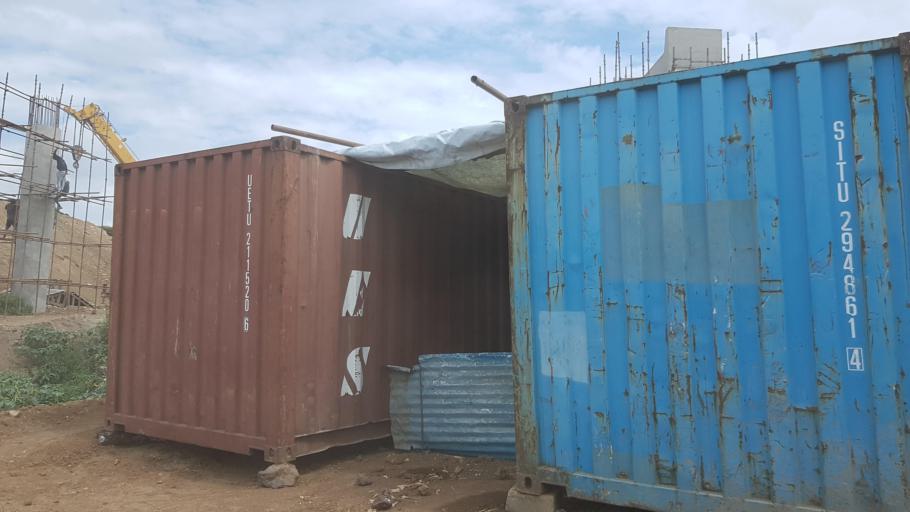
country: ET
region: Oromiya
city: Shashemene
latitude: 7.2375
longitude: 38.5769
